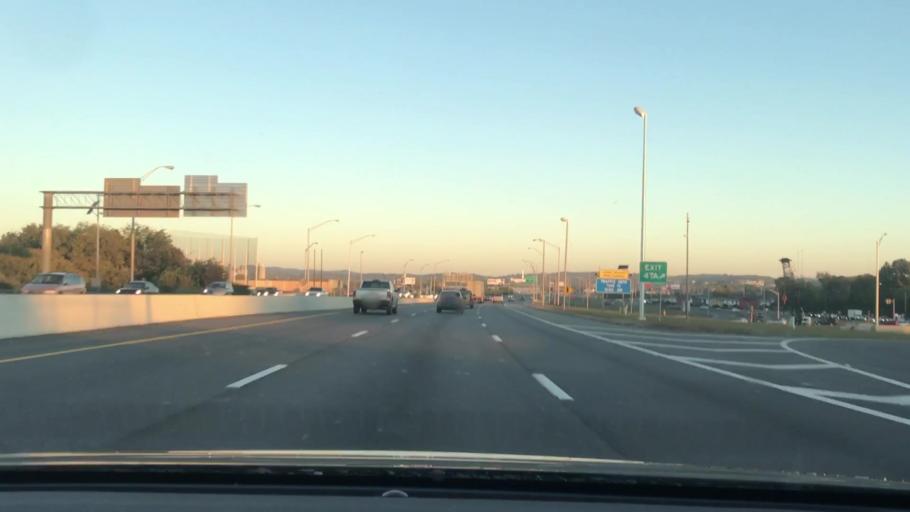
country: US
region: Tennessee
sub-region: Davidson County
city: Nashville
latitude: 36.1747
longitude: -86.7709
